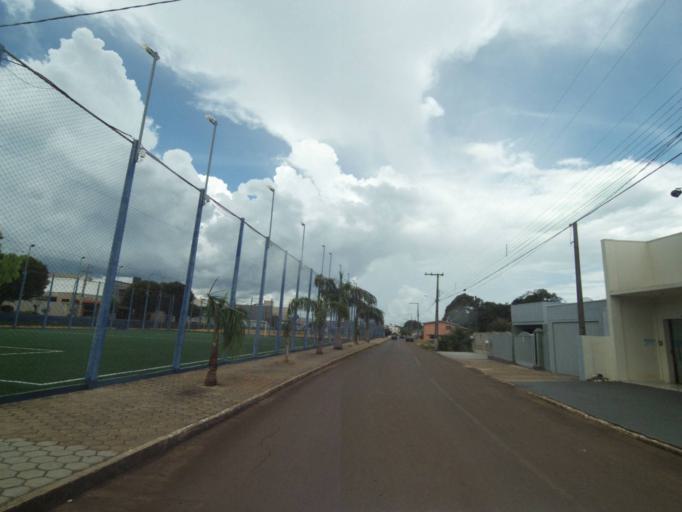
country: BR
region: Parana
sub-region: Guaraniacu
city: Guaraniacu
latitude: -25.0980
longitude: -52.8729
